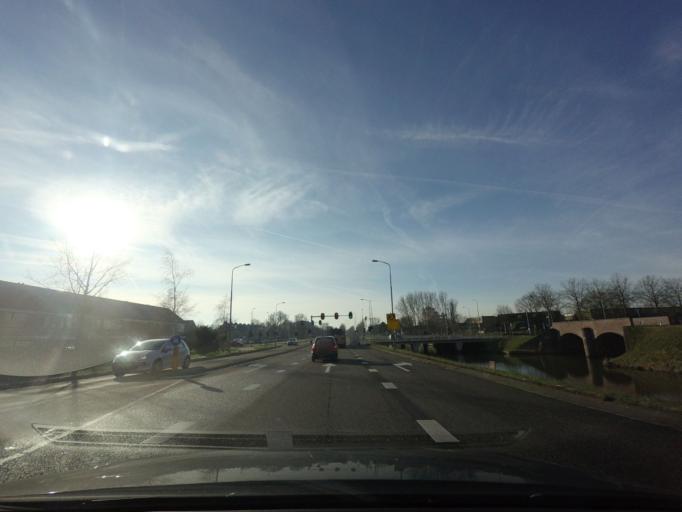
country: NL
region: North Holland
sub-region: Gemeente Haarlemmermeer
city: Hoofddorp
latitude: 52.3007
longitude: 4.6861
